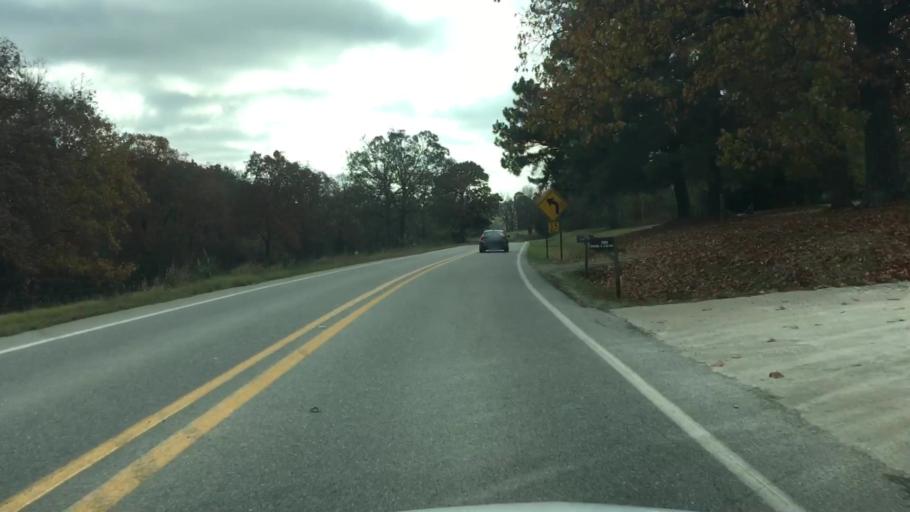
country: US
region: Arkansas
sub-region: Benton County
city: Gentry
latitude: 36.2596
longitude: -94.4500
